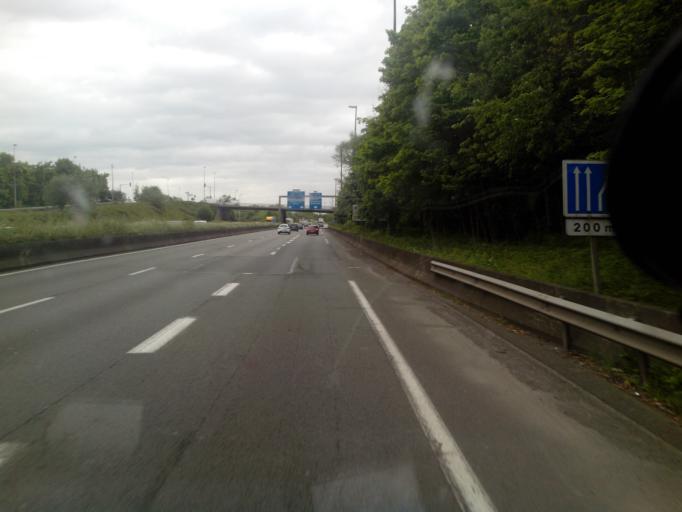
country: FR
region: Nord-Pas-de-Calais
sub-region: Departement du Nord
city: Mons-en-Baroeul
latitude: 50.6535
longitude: 3.1060
